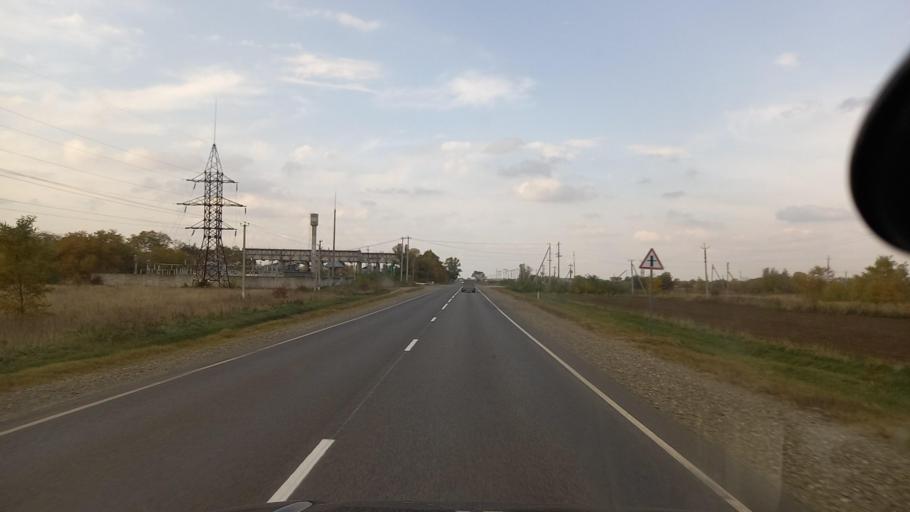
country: RU
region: Krasnodarskiy
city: Mostovskoy
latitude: 44.3731
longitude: 40.8260
